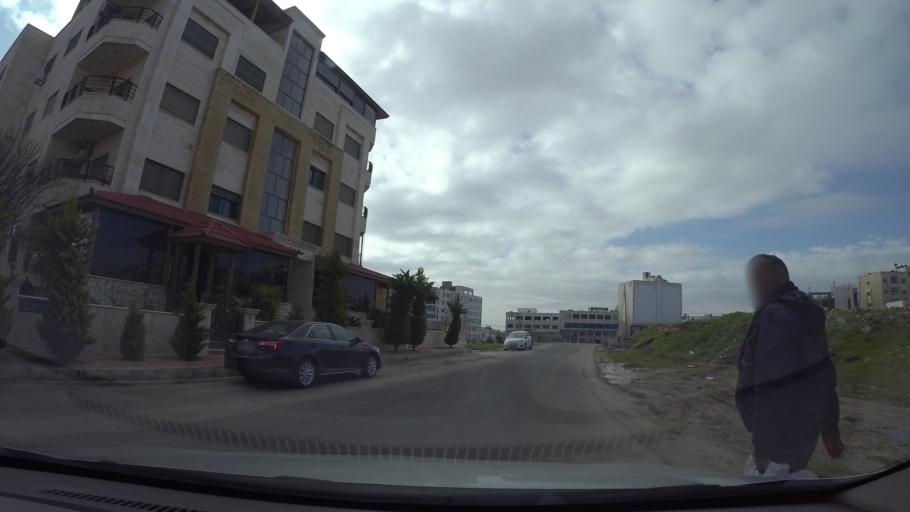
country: JO
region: Amman
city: Al Jubayhah
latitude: 31.9985
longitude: 35.8434
